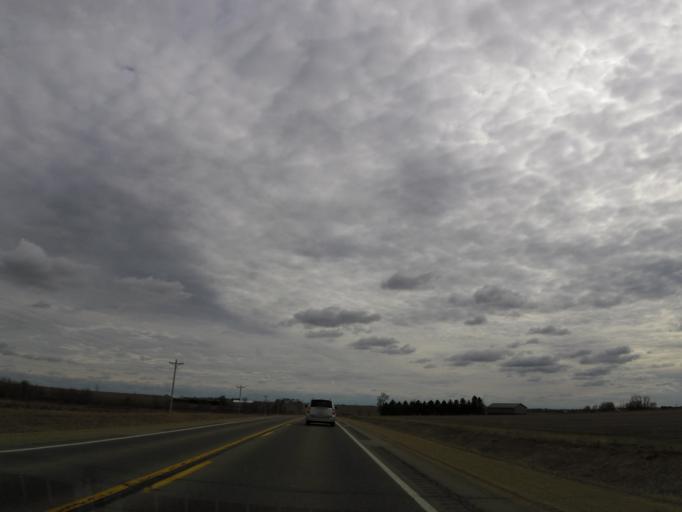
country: US
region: Iowa
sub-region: Chickasaw County
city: New Hampton
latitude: 43.1476
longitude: -92.2990
